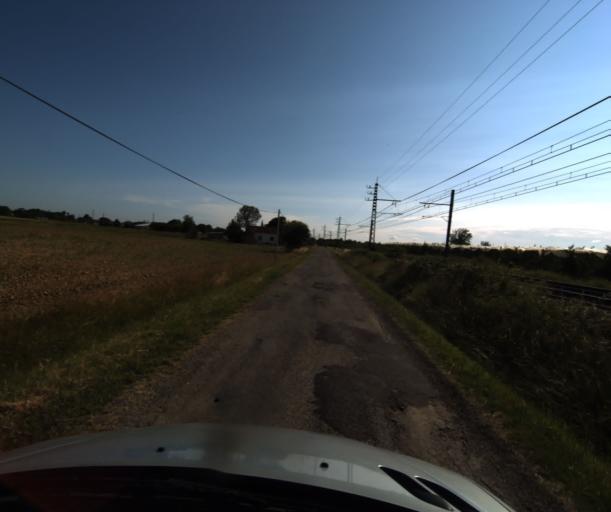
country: FR
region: Midi-Pyrenees
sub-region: Departement du Tarn-et-Garonne
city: Bressols
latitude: 43.9703
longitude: 1.3094
